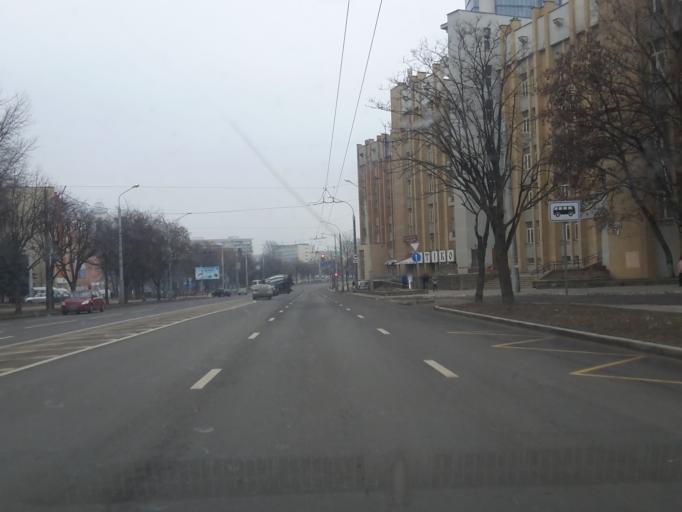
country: BY
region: Minsk
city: Minsk
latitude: 53.9085
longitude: 27.5301
